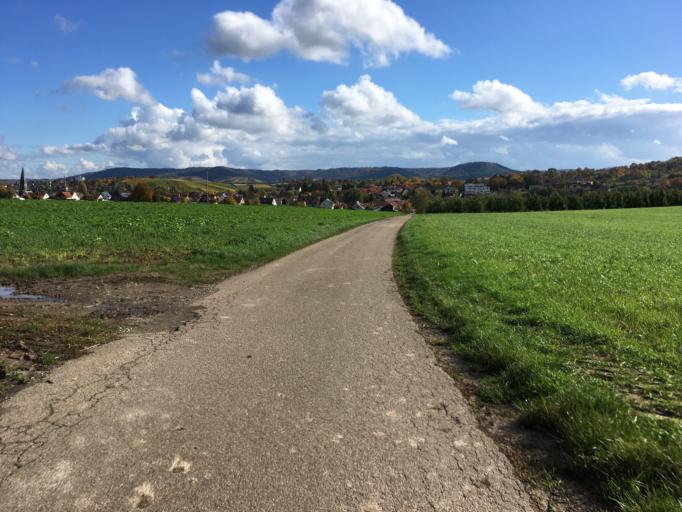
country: DE
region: Baden-Wuerttemberg
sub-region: Regierungsbezirk Stuttgart
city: Pfedelbach
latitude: 49.1755
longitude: 9.4933
